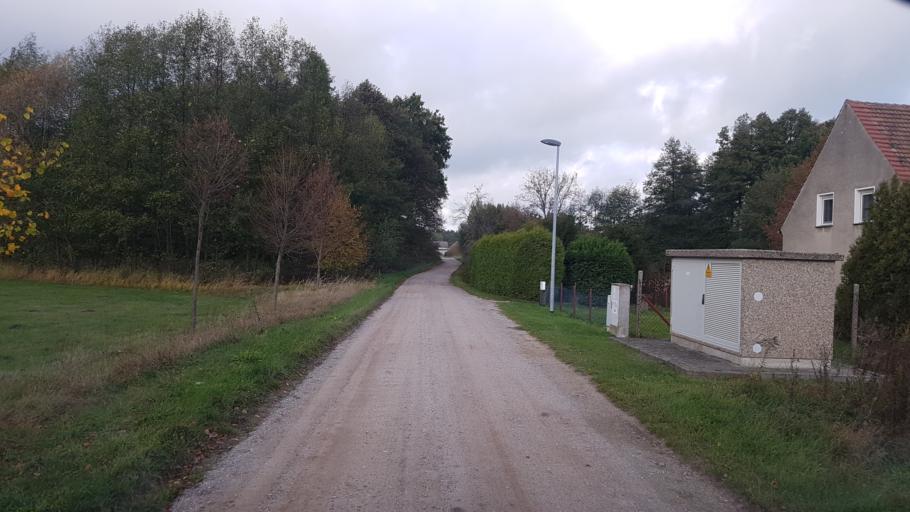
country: DE
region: Brandenburg
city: Schonborn
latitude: 51.6140
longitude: 13.5151
